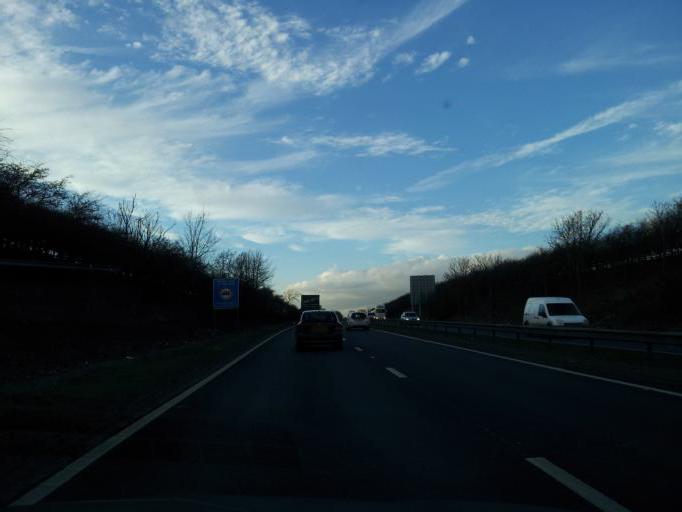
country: GB
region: England
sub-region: District of Rutland
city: Tinwell
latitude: 52.6497
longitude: -0.5088
